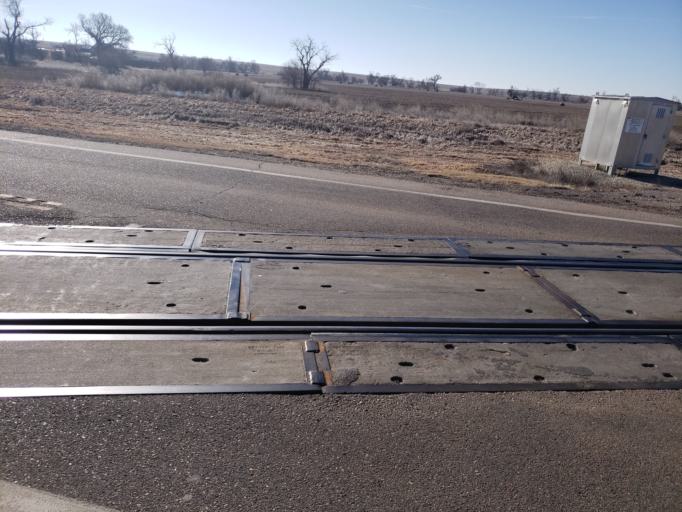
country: US
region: Kansas
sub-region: Ness County
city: Ness City
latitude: 38.4533
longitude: -99.6474
